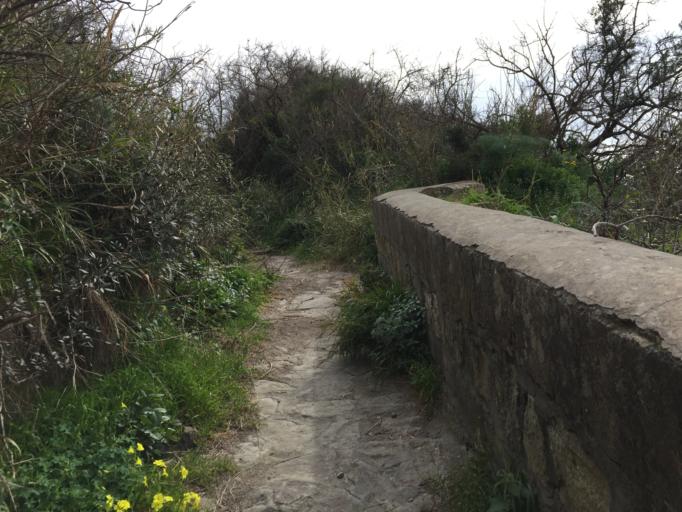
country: IT
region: Campania
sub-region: Provincia di Napoli
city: Bacoli
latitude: 40.7817
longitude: 14.0864
